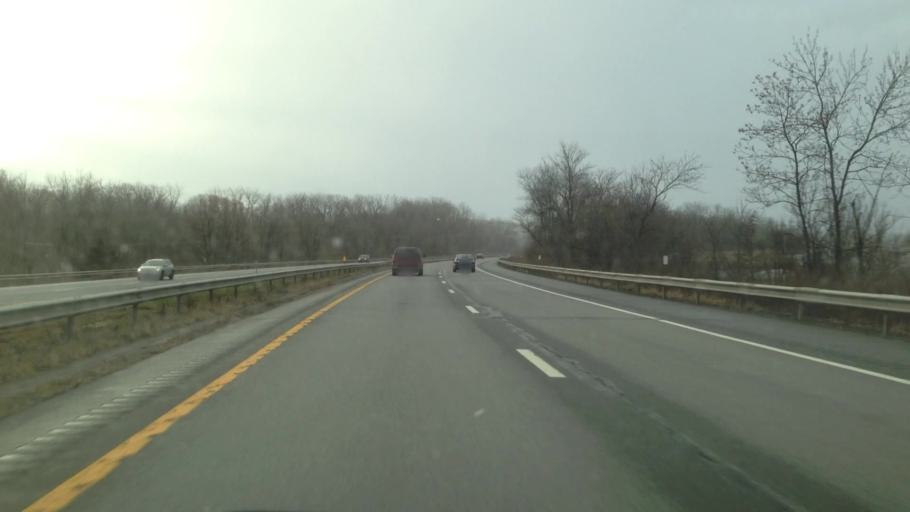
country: US
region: New York
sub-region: Montgomery County
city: Tribes Hill
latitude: 42.9300
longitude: -74.3035
